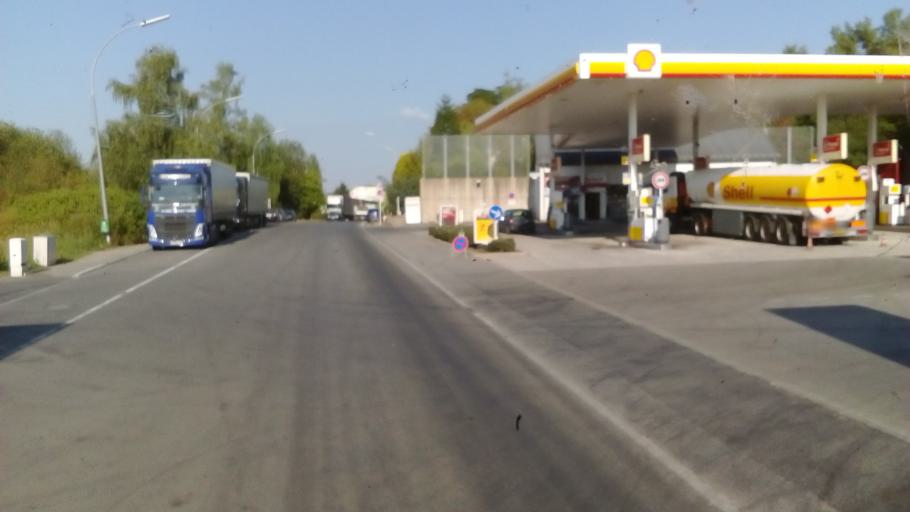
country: FR
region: Lorraine
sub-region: Departement de Meurthe-et-Moselle
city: Saulnes
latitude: 49.5430
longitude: 5.8181
